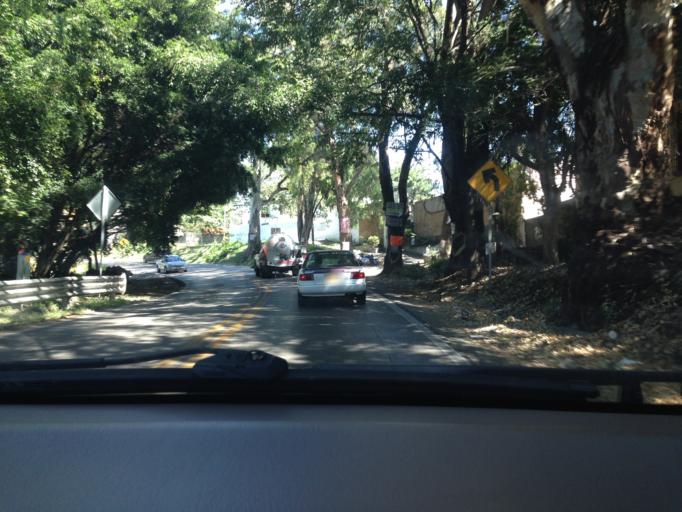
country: MX
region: Morelos
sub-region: Cuernavaca
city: Fraccionamiento Lomas de Ahuatlan
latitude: 18.9750
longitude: -99.2523
